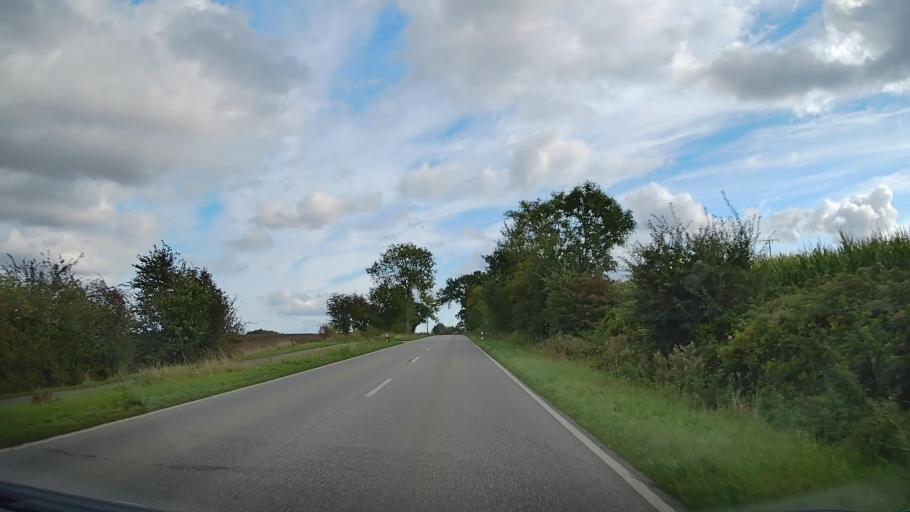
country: DE
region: Schleswig-Holstein
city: Niesgrau
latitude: 54.7537
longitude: 9.8089
